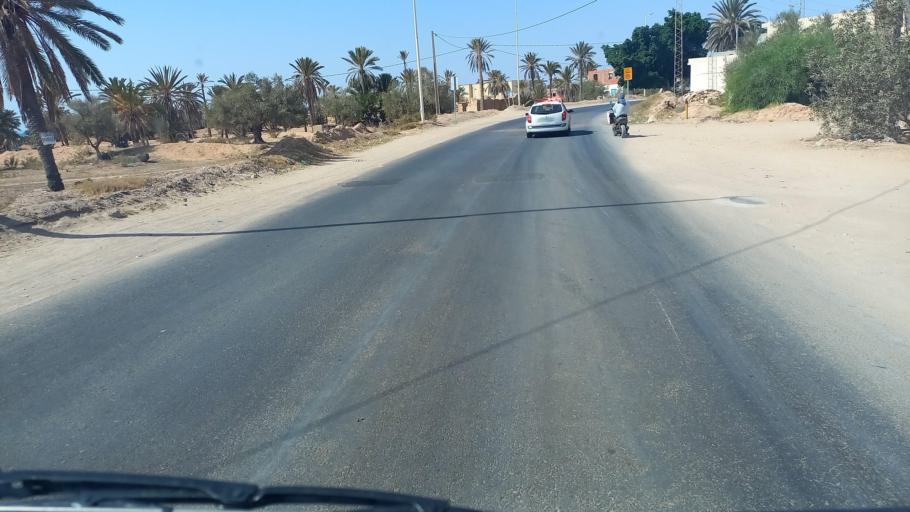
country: TN
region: Madanin
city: Midoun
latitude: 33.7779
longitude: 11.0385
